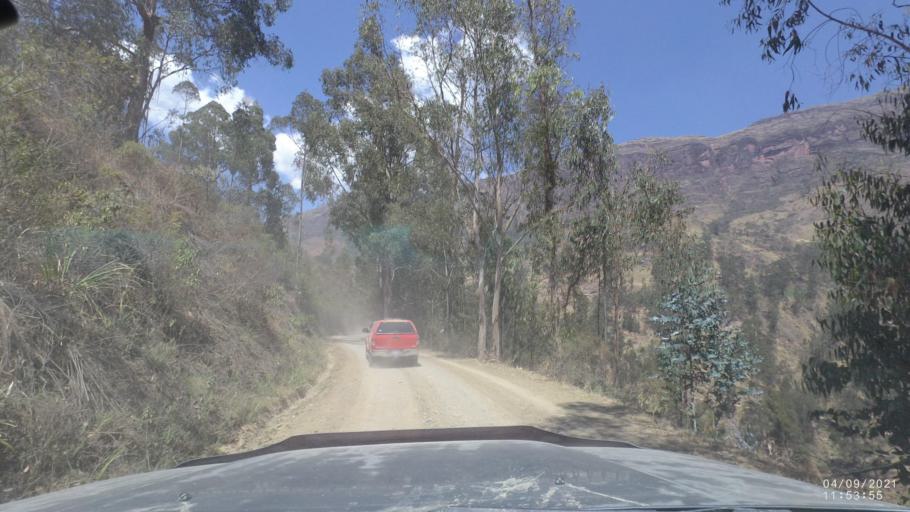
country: BO
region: Cochabamba
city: Colchani
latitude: -17.2356
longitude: -66.5261
